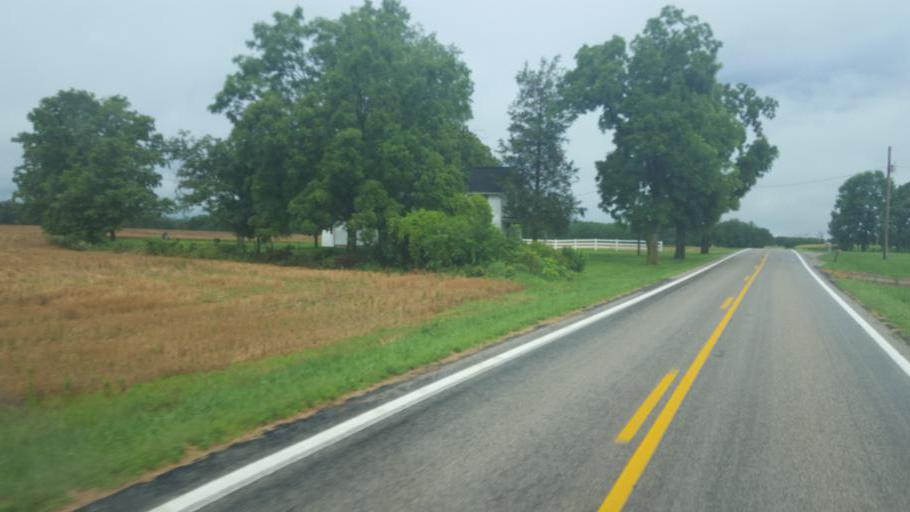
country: US
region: Ohio
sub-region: Union County
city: Richwood
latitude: 40.5542
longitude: -83.3754
